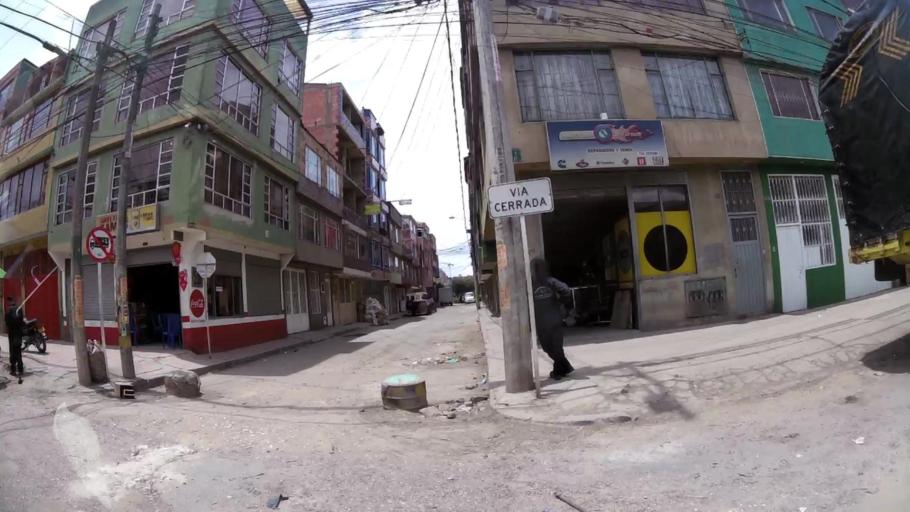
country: CO
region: Bogota D.C.
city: Bogota
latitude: 4.6449
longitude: -74.1499
